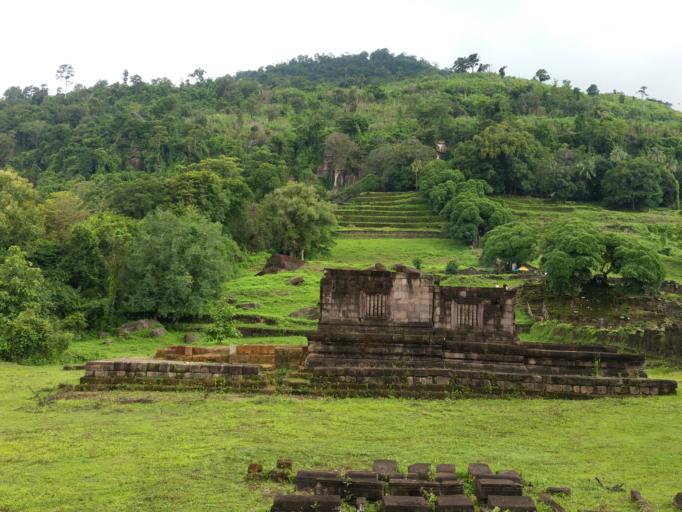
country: LA
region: Champasak
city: Champasak
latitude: 14.8480
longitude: 105.8174
